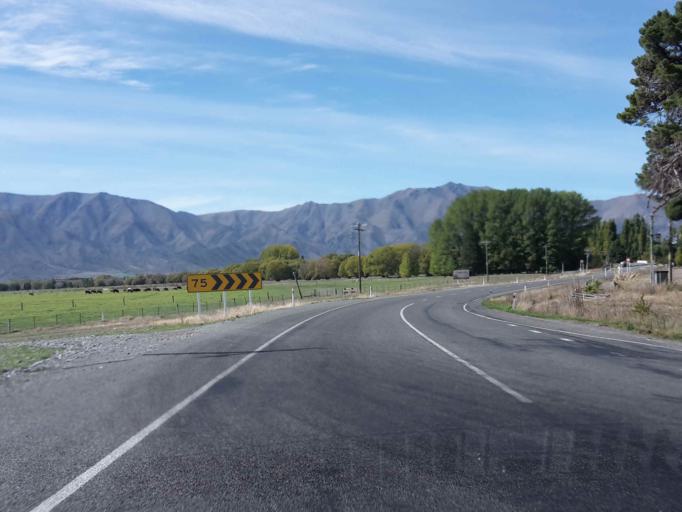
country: NZ
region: Otago
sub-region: Queenstown-Lakes District
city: Wanaka
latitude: -44.4889
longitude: 169.9522
